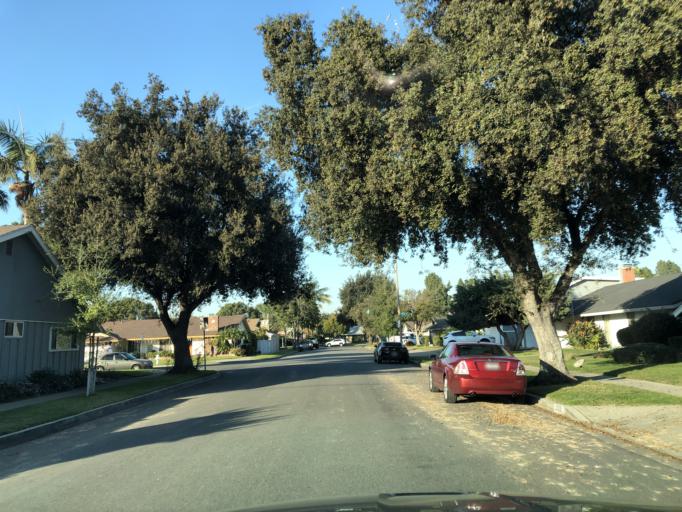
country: US
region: California
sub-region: Orange County
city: Tustin
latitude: 33.7627
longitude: -117.8450
